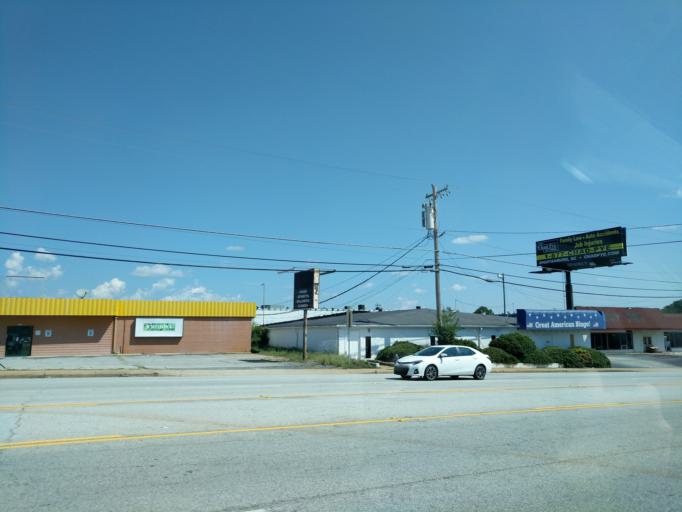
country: US
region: South Carolina
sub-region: Spartanburg County
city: Saxon
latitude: 34.9789
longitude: -81.9650
